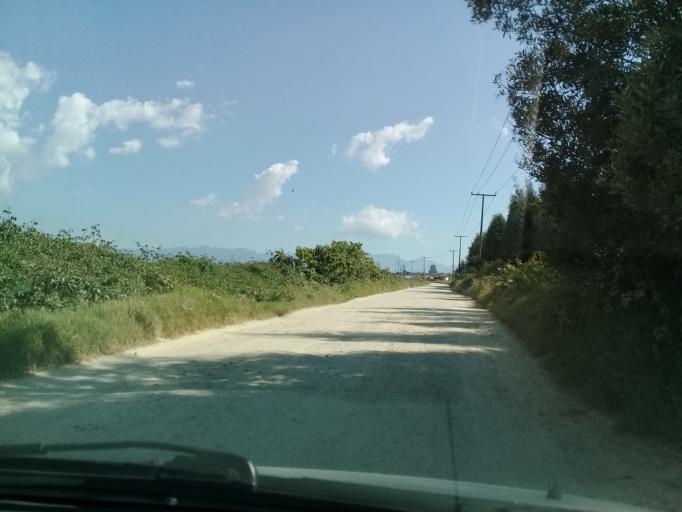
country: CO
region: Cundinamarca
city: Funza
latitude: 4.7314
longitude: -74.1967
